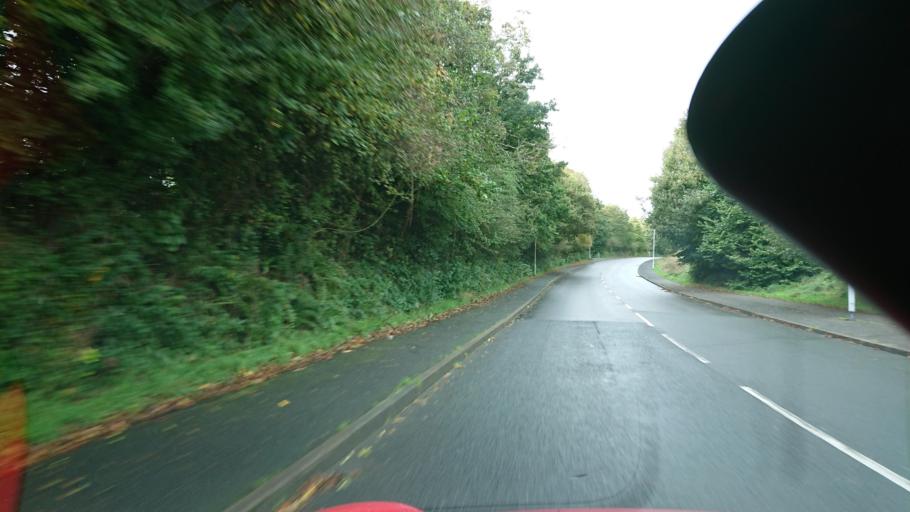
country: GB
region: England
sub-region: Plymouth
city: Plymouth
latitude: 50.3966
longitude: -4.1224
